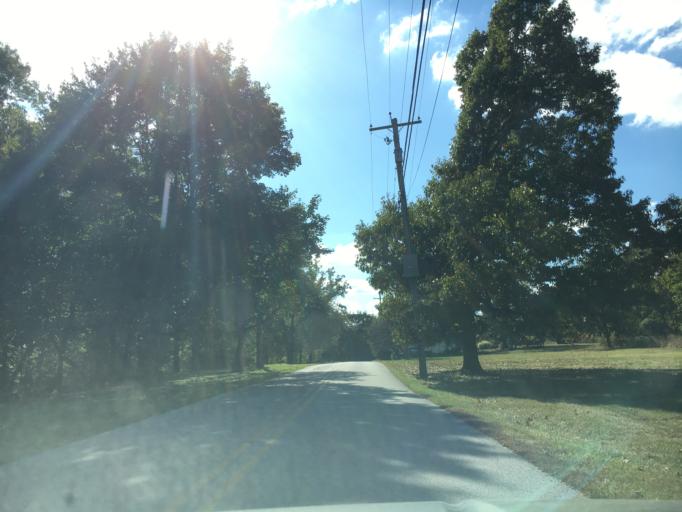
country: US
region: Pennsylvania
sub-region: York County
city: Yorklyn
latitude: 40.0051
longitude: -76.6746
